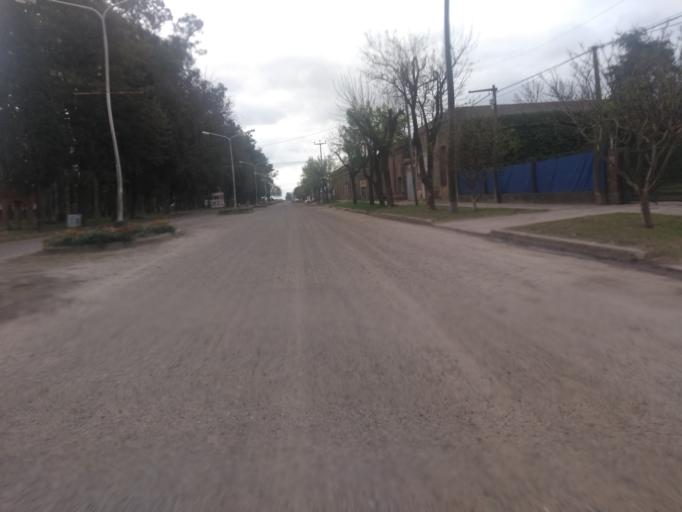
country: AR
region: Santa Fe
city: Galvez
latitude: -31.9066
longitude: -61.2802
